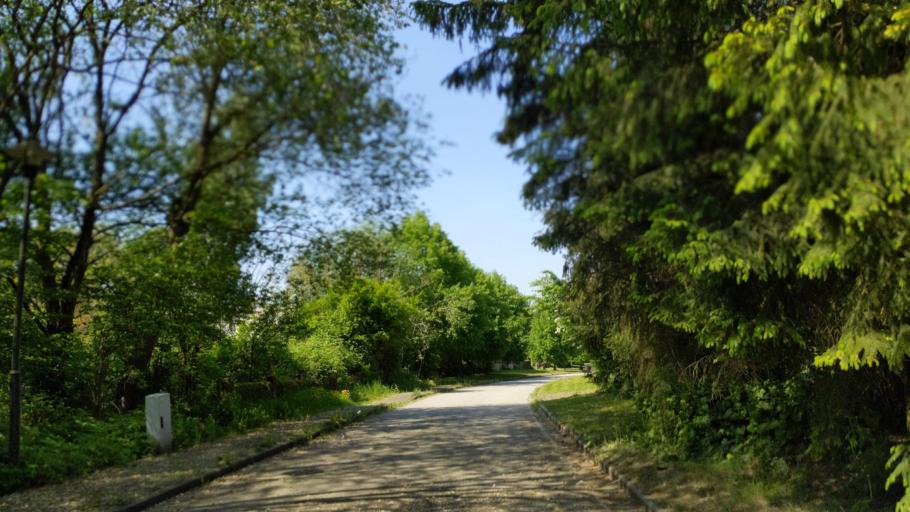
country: DE
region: Mecklenburg-Vorpommern
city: Selmsdorf
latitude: 53.8819
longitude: 10.8928
